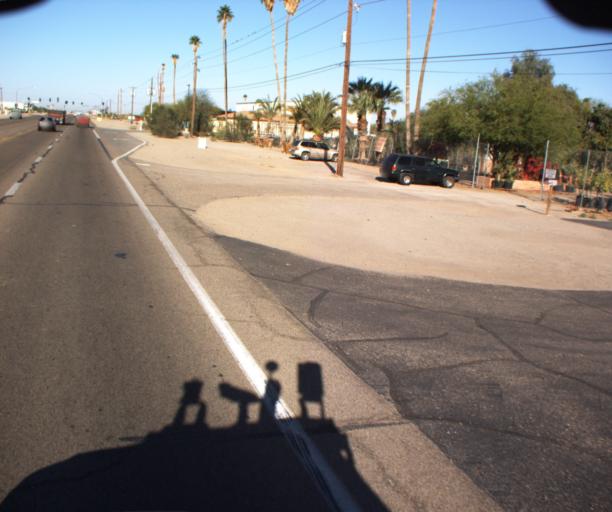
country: US
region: Arizona
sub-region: Yuma County
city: Yuma
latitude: 32.6699
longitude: -114.5613
